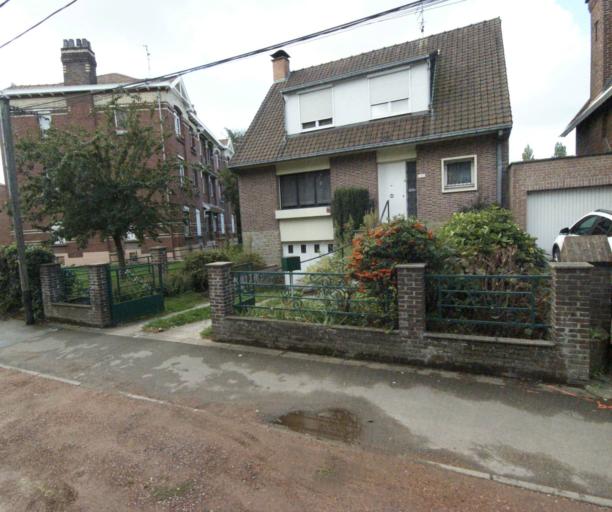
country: FR
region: Nord-Pas-de-Calais
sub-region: Departement du Nord
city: Loos
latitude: 50.6197
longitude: 3.0168
